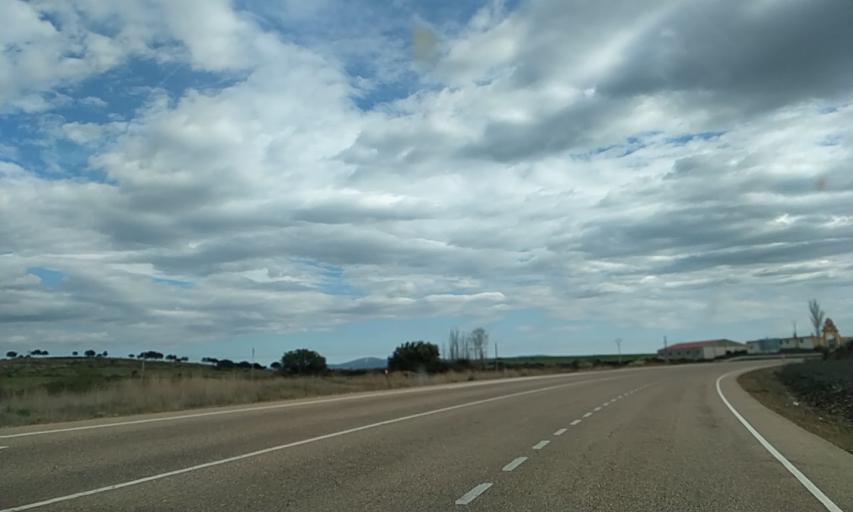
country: ES
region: Castille and Leon
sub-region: Provincia de Salamanca
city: Herguijuela de Ciudad Rodrigo
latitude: 40.4806
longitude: -6.5778
